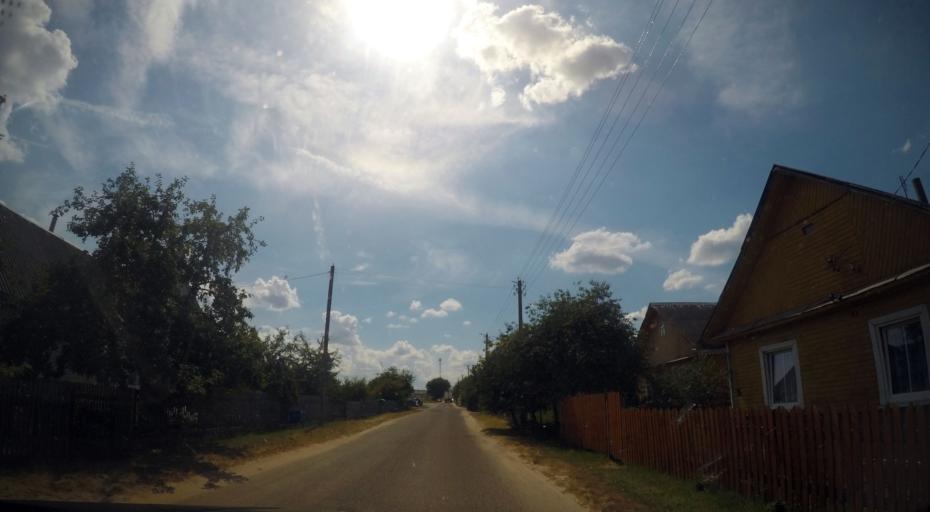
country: BY
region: Grodnenskaya
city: Hrodna
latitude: 53.6250
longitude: 23.8381
